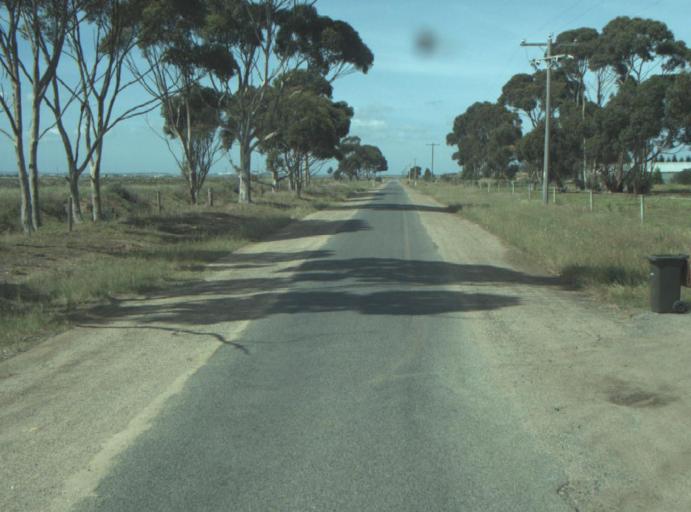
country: AU
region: Victoria
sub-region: Greater Geelong
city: Lara
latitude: -38.0685
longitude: 144.4253
